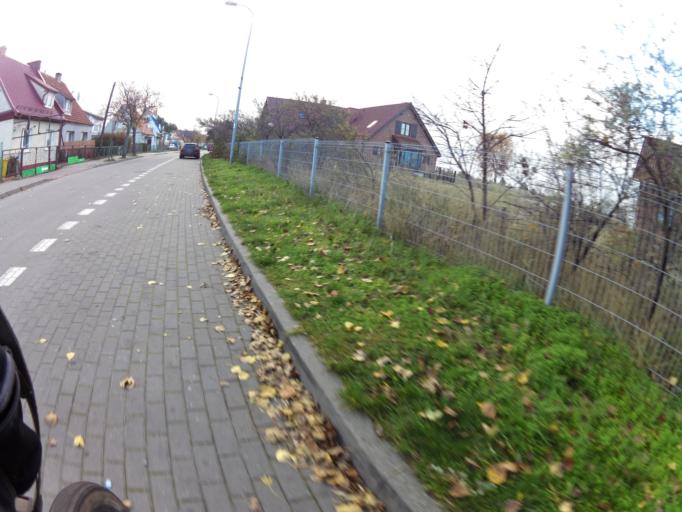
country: PL
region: Pomeranian Voivodeship
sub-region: Powiat pucki
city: Hel
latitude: 54.6091
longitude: 18.7974
